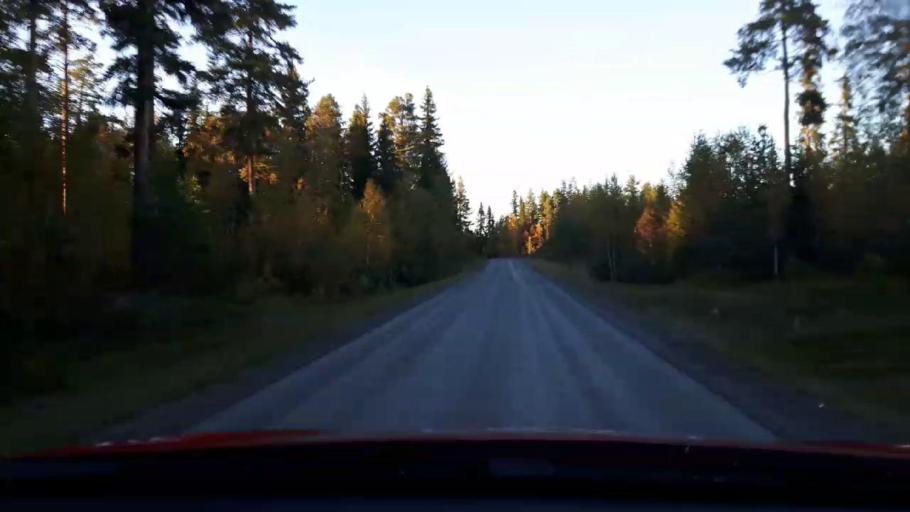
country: SE
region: Jaemtland
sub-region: Krokoms Kommun
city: Krokom
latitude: 63.4425
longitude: 14.4220
